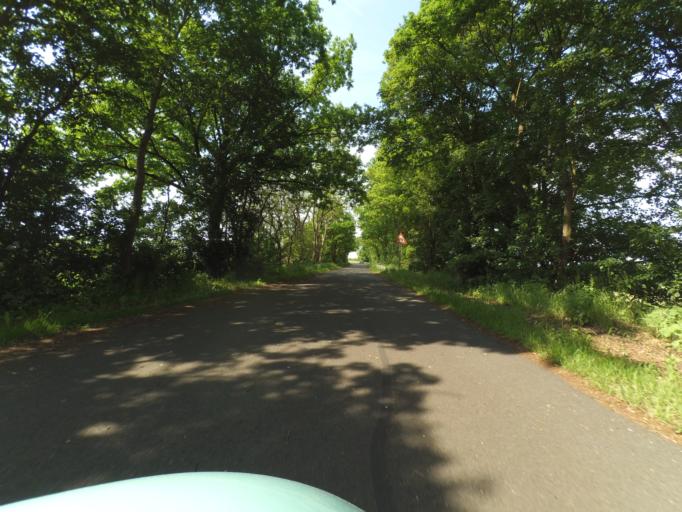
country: DE
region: Lower Saxony
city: Lehrte
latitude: 52.3906
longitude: 9.9863
